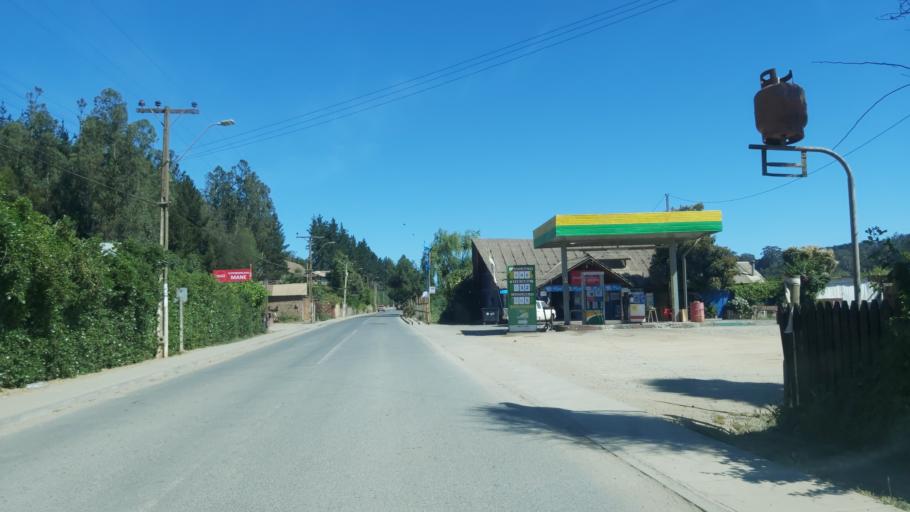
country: CL
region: Maule
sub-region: Provincia de Talca
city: Constitucion
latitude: -34.7748
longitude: -72.0635
